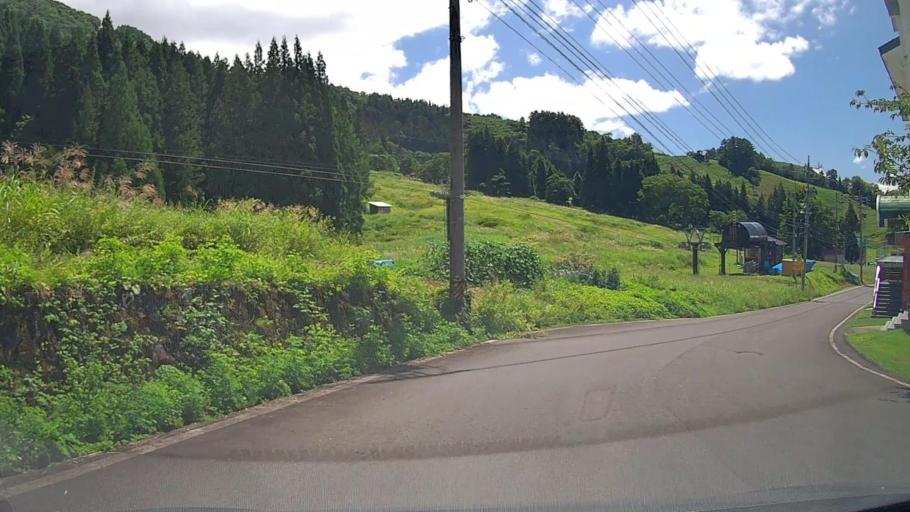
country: JP
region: Nagano
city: Iiyama
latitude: 36.9279
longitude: 138.4561
